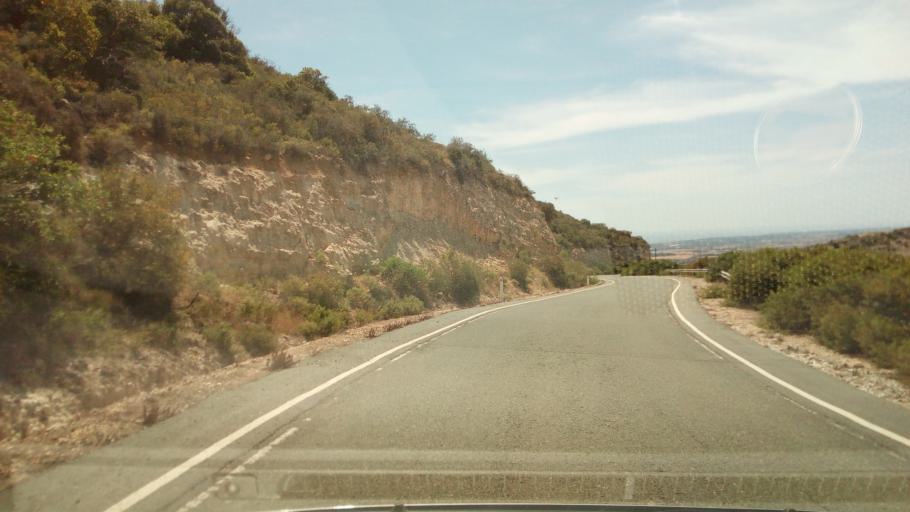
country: CY
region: Limassol
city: Pissouri
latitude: 34.7263
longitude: 32.6169
